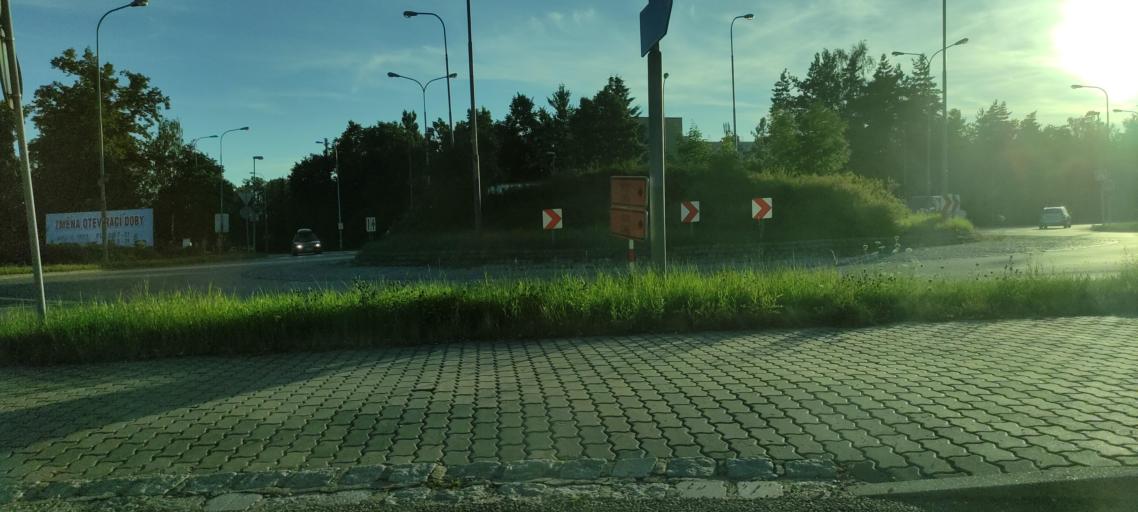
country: CZ
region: Jihocesky
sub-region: Okres Jindrichuv Hradec
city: Jindrichuv Hradec
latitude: 49.1518
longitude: 15.0110
